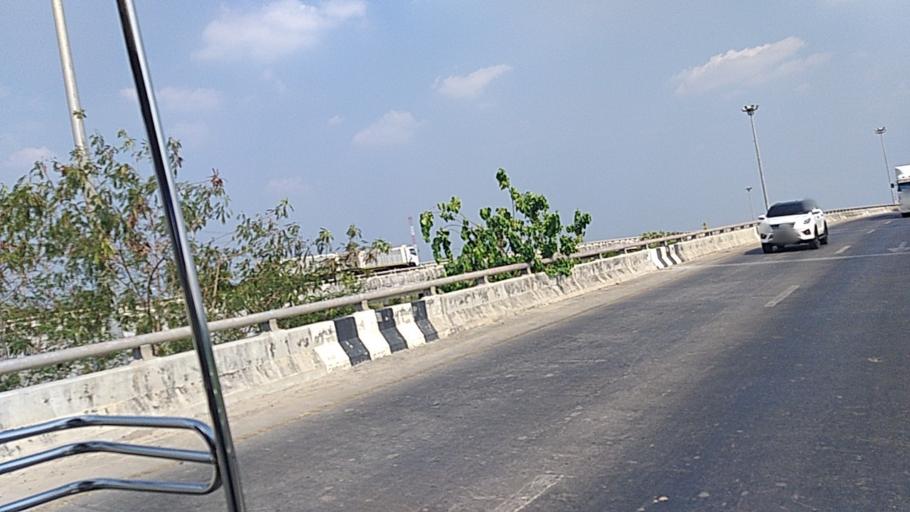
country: TH
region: Pathum Thani
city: Sam Khok
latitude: 14.0951
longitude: 100.5174
